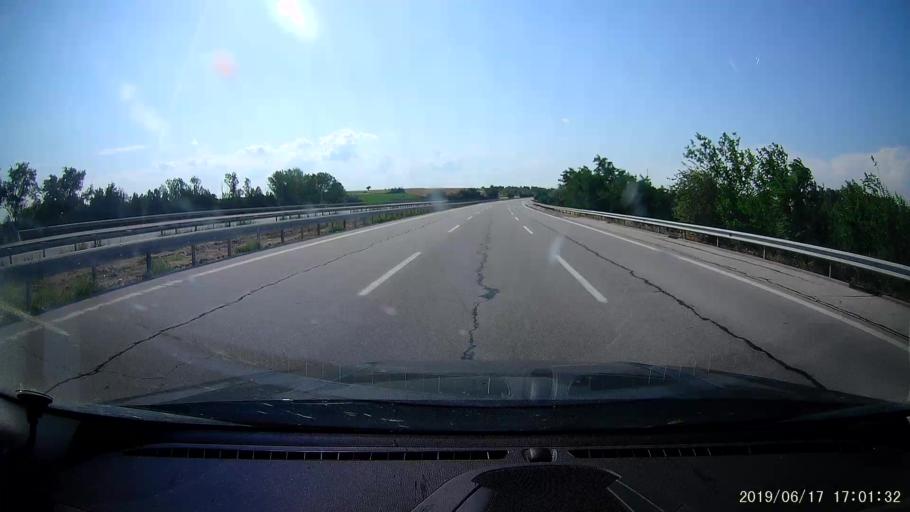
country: TR
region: Edirne
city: Haskoy
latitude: 41.6297
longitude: 26.8021
